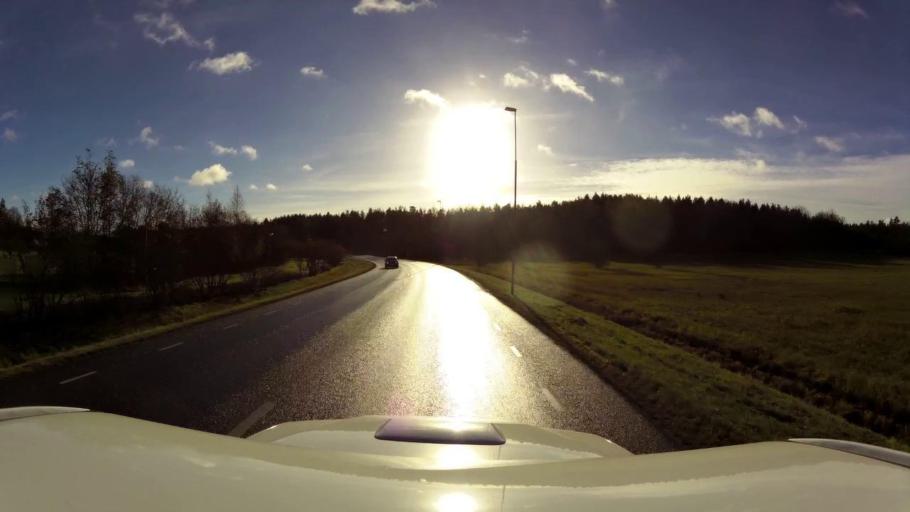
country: SE
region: OEstergoetland
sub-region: Linkopings Kommun
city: Linkoping
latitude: 58.3779
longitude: 15.6358
